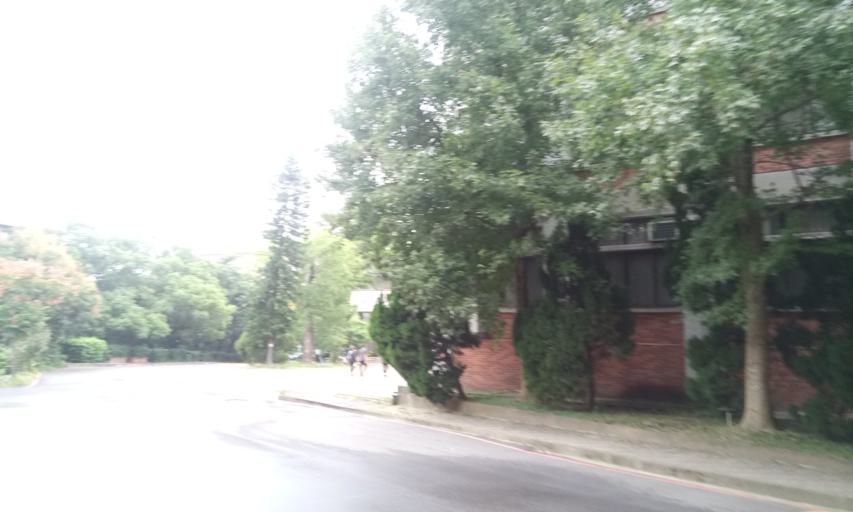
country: TW
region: Taiwan
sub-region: Hsinchu
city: Hsinchu
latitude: 24.7572
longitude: 120.9538
